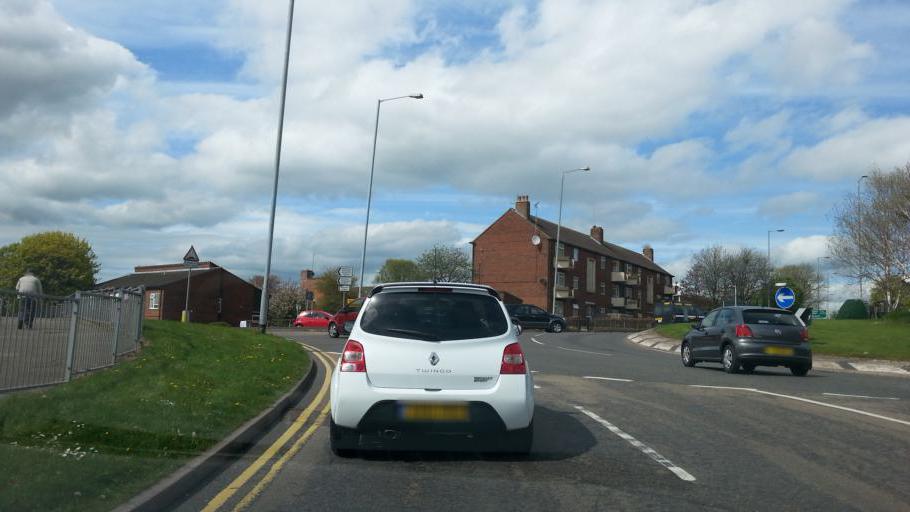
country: GB
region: England
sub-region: Staffordshire
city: Newcastle under Lyme
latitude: 53.0132
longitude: -2.2313
